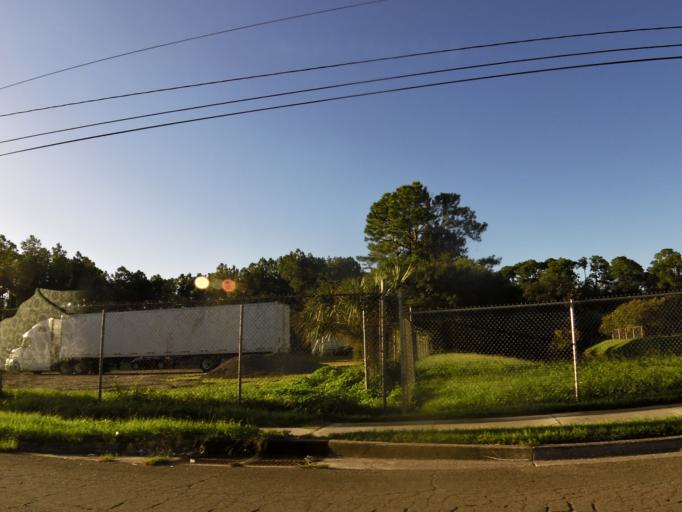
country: US
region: Florida
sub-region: Duval County
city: Jacksonville
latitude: 30.3622
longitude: -81.7023
